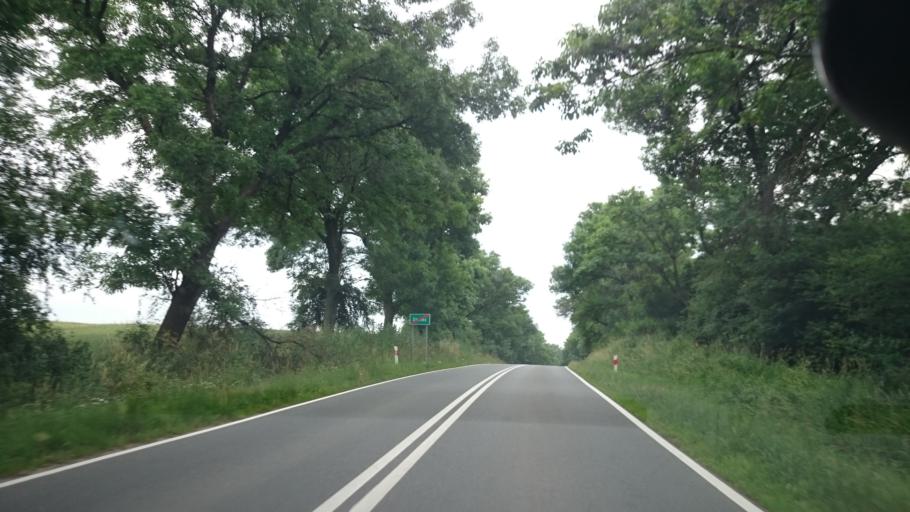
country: PL
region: Lower Silesian Voivodeship
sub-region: Powiat zabkowicki
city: Kamieniec Zabkowicki
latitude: 50.5847
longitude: 16.8876
